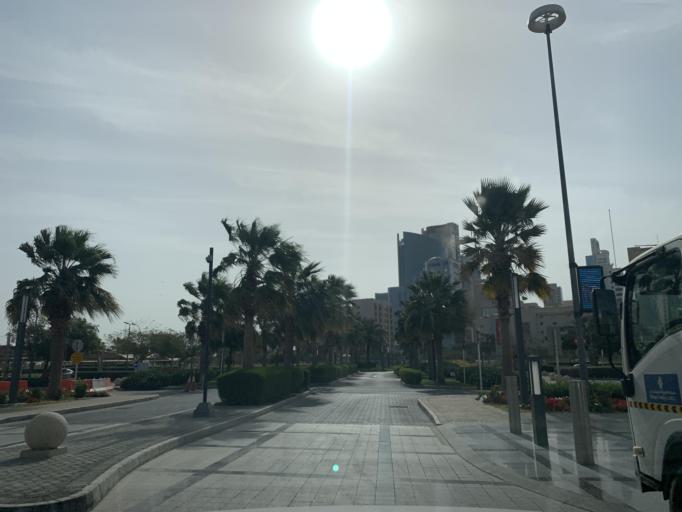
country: BH
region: Muharraq
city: Al Muharraq
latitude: 26.2453
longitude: 50.5857
